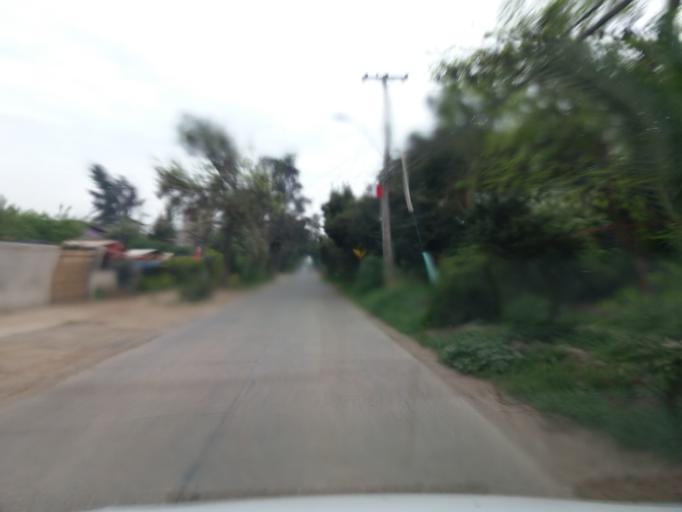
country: CL
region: Valparaiso
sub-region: Provincia de Quillota
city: Hacienda La Calera
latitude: -32.8185
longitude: -71.1348
